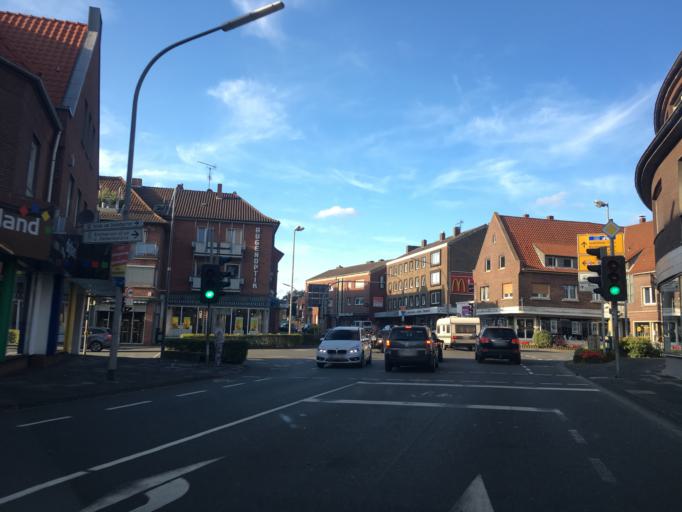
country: DE
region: North Rhine-Westphalia
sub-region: Regierungsbezirk Munster
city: Dulmen
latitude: 51.8281
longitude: 7.2787
